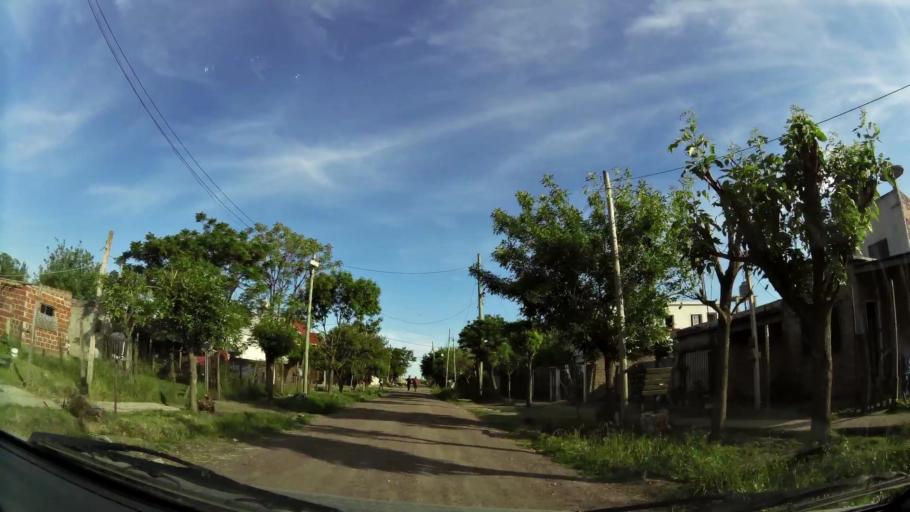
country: AR
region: Buenos Aires
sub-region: Partido de Almirante Brown
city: Adrogue
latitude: -34.8173
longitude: -58.3218
